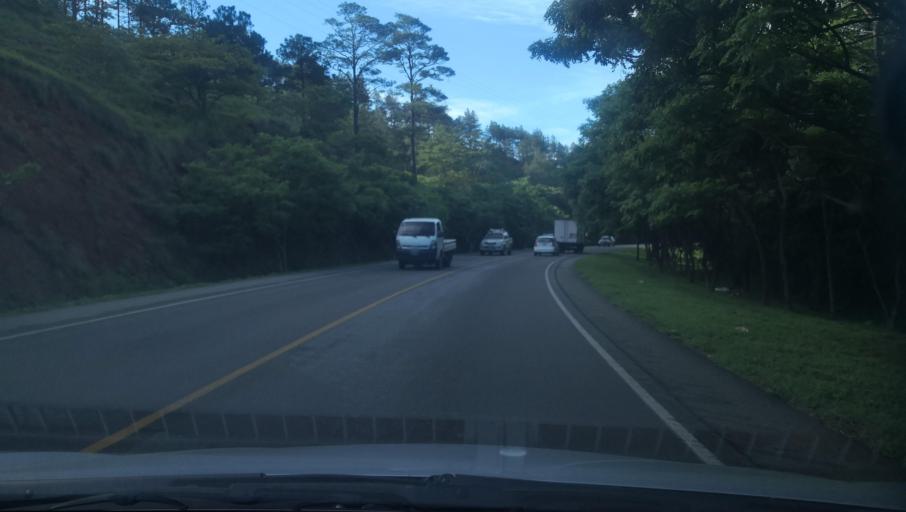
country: NI
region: Madriz
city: Totogalpa
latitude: 13.5719
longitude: -86.4832
